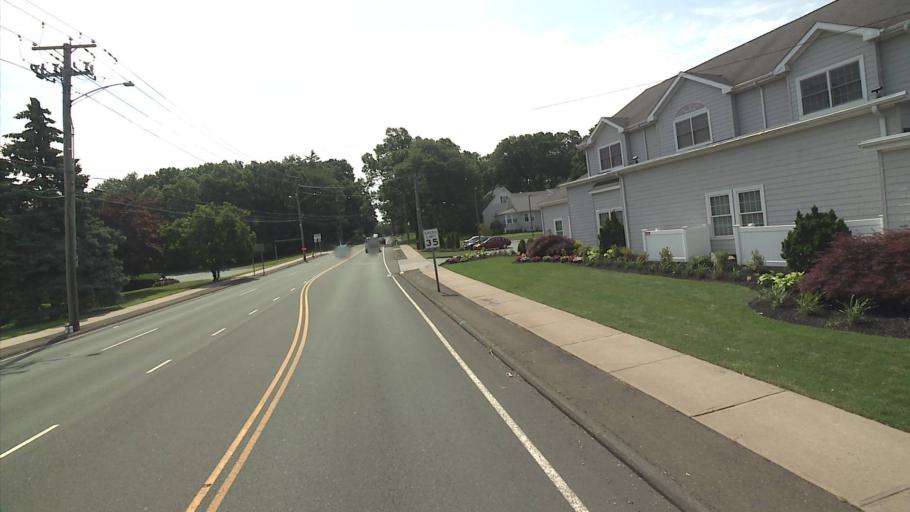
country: US
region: Connecticut
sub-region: New Haven County
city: North Haven
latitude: 41.3906
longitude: -72.8592
